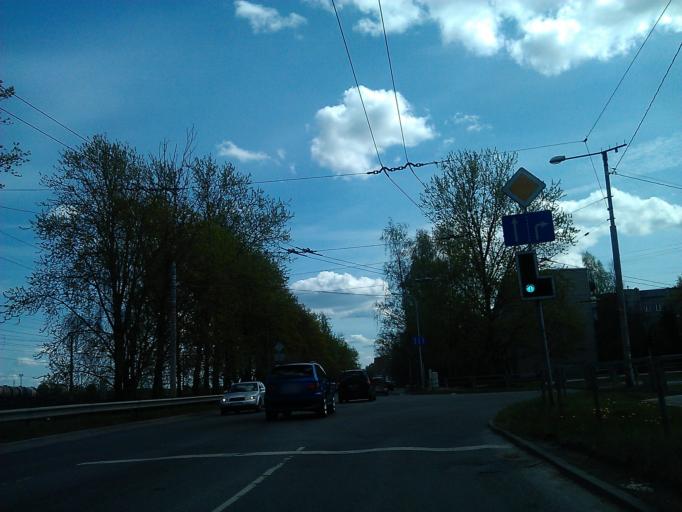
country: LV
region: Kekava
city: Balozi
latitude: 56.9174
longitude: 24.1871
